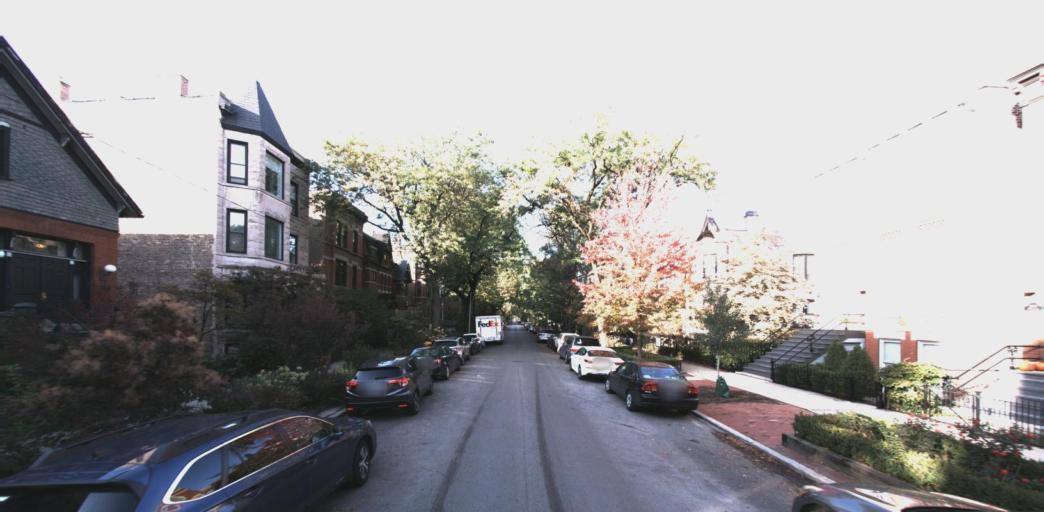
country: US
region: Illinois
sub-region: Cook County
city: Chicago
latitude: 41.9186
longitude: -87.6558
